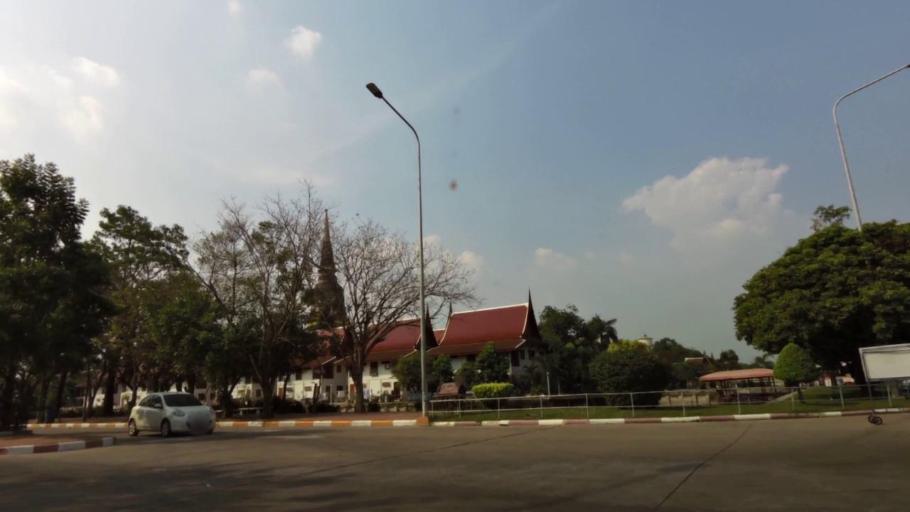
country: TH
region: Phra Nakhon Si Ayutthaya
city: Phra Nakhon Si Ayutthaya
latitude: 14.3442
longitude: 100.5941
